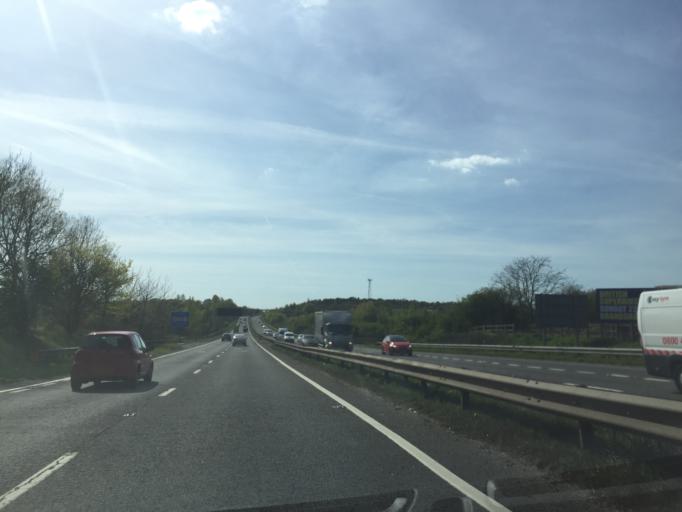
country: GB
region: England
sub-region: Greater London
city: Bexley
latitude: 51.4094
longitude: 0.1426
